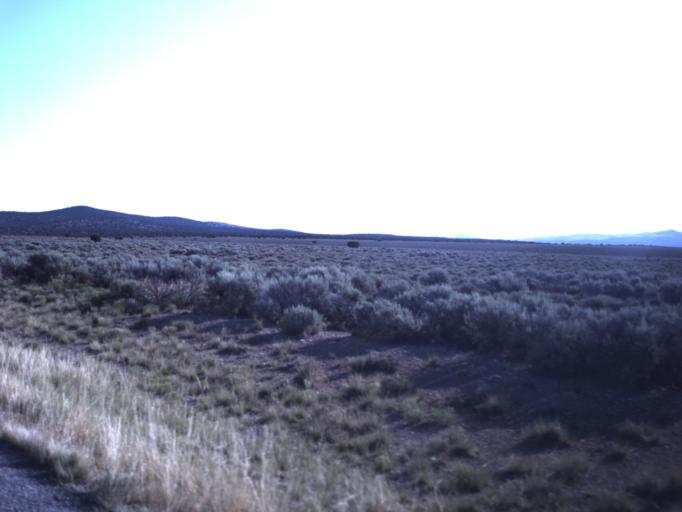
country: US
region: Utah
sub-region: Iron County
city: Enoch
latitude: 38.0042
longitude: -112.9978
